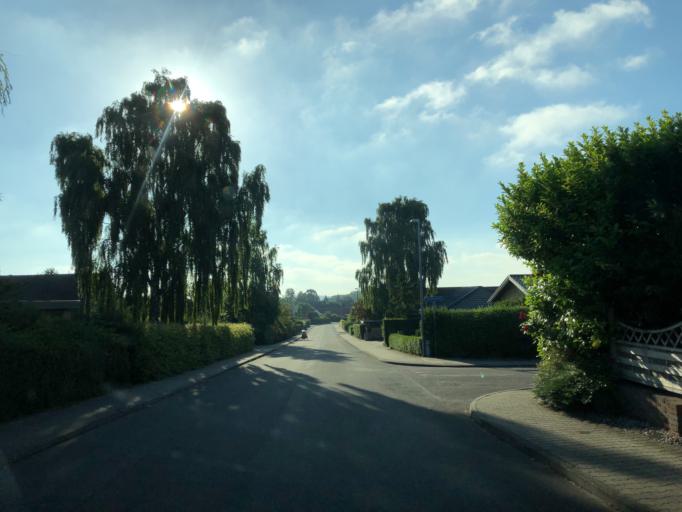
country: DK
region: South Denmark
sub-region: Vejle Kommune
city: Borkop
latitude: 55.6014
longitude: 9.6570
